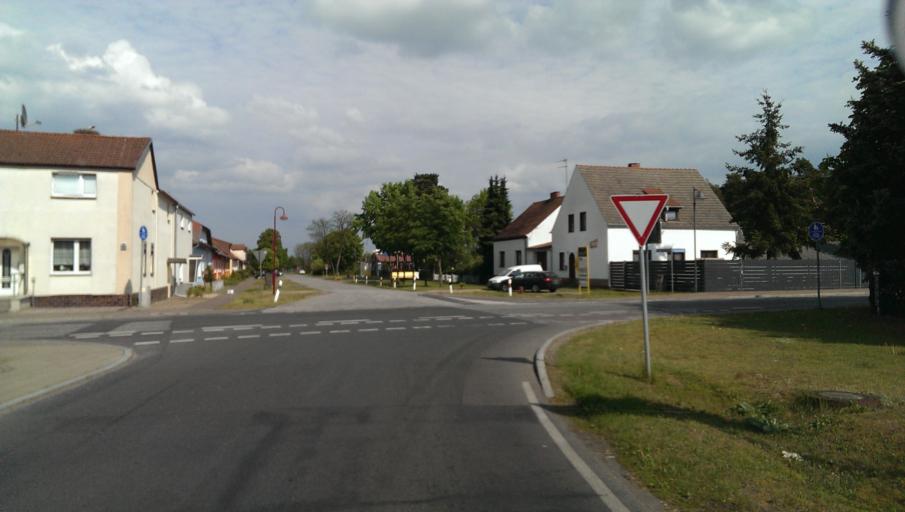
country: DE
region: Brandenburg
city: Bruck
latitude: 52.1780
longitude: 12.7571
